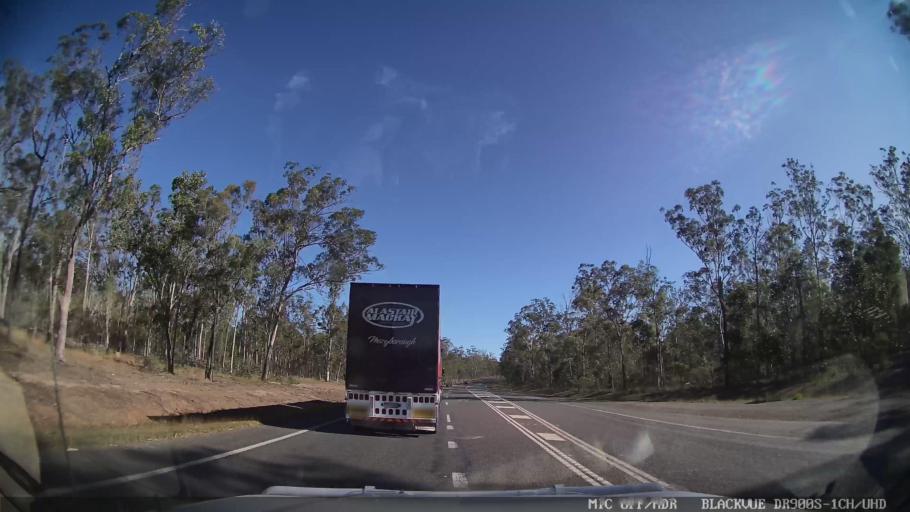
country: AU
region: Queensland
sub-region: Bundaberg
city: Childers
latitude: -25.2123
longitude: 152.0825
